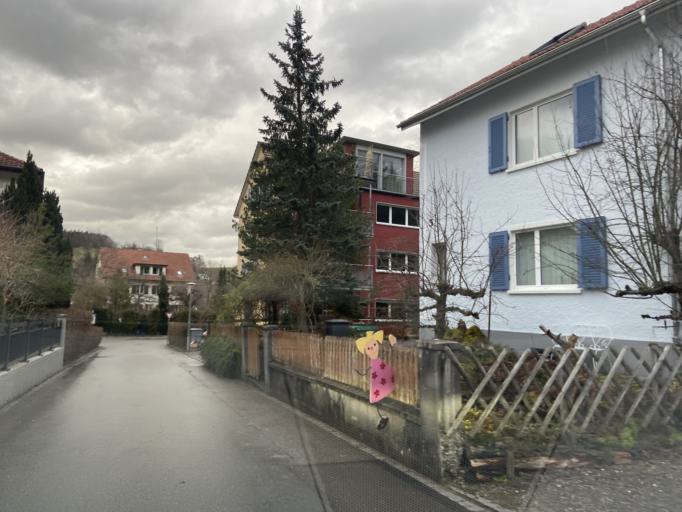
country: CH
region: Zurich
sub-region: Bezirk Winterthur
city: Wuelflingen (Kreis 6) / Oberfeld
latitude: 47.5055
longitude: 8.7055
